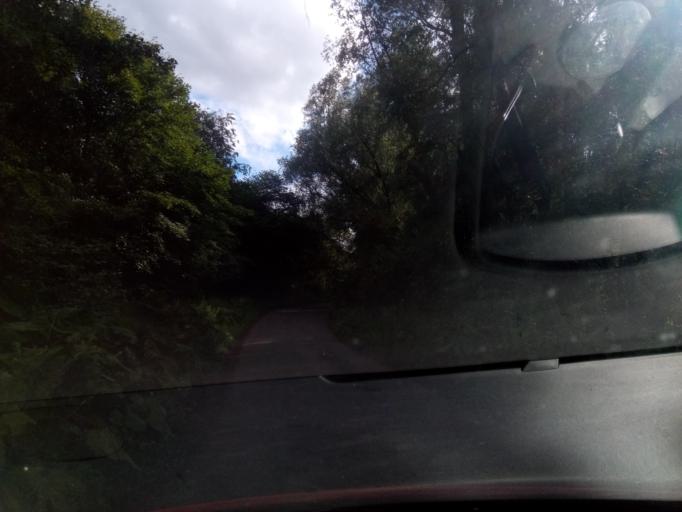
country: GB
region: Scotland
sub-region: The Scottish Borders
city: Coldstream
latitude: 55.5876
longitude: -2.2546
